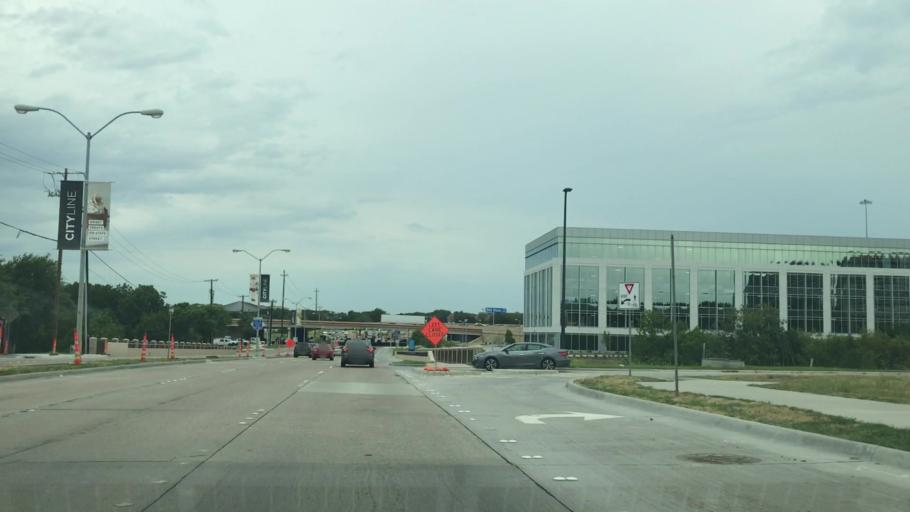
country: US
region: Texas
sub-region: Collin County
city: Plano
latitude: 32.9973
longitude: -96.7054
